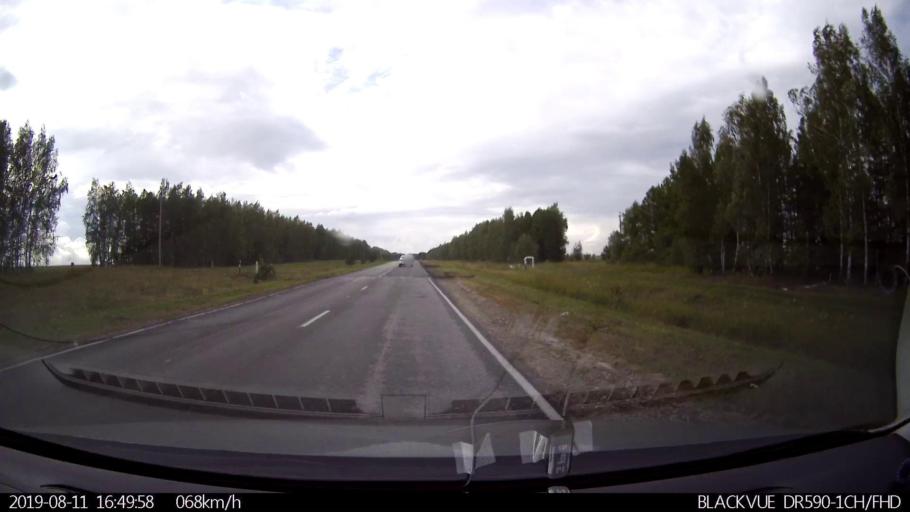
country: RU
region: Ulyanovsk
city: Mayna
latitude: 54.2249
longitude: 47.6925
